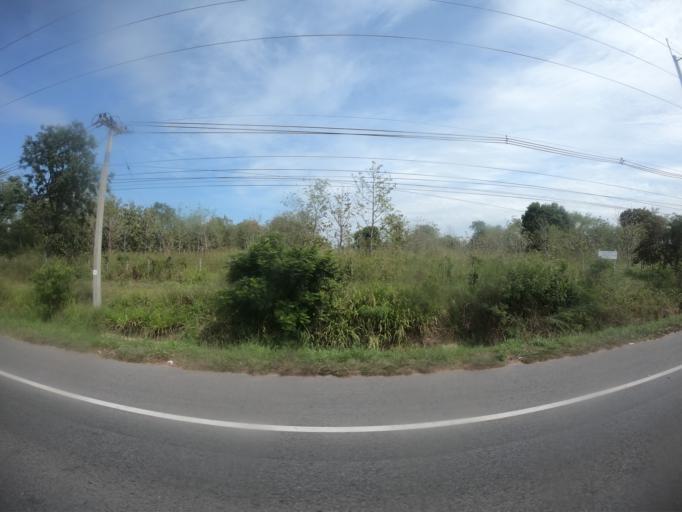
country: TH
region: Maha Sarakham
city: Chiang Yuen
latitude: 16.4350
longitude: 103.0536
